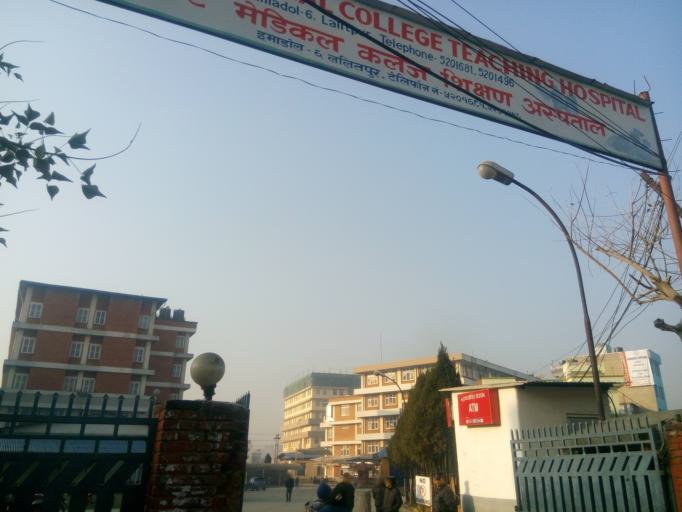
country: NP
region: Central Region
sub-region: Bagmati Zone
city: Patan
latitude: 27.6638
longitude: 85.3359
